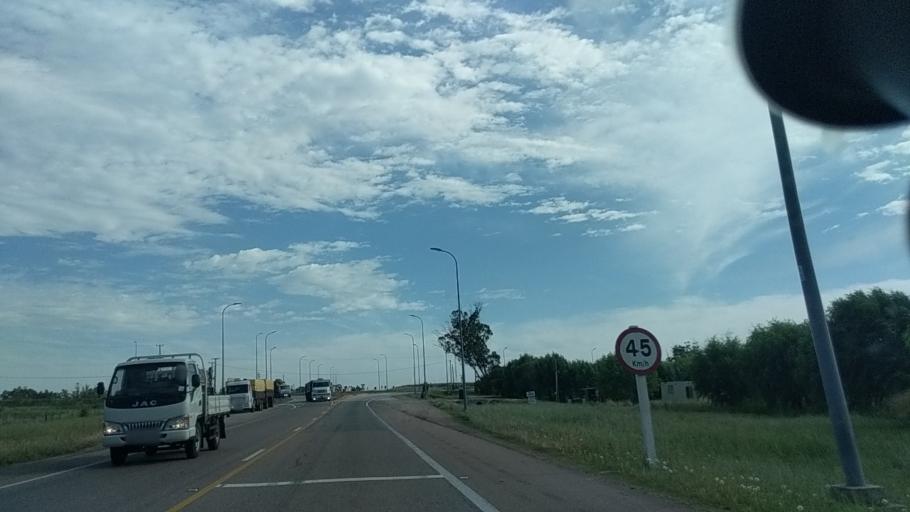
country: UY
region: Canelones
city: Canelones
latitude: -34.4232
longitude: -56.2628
